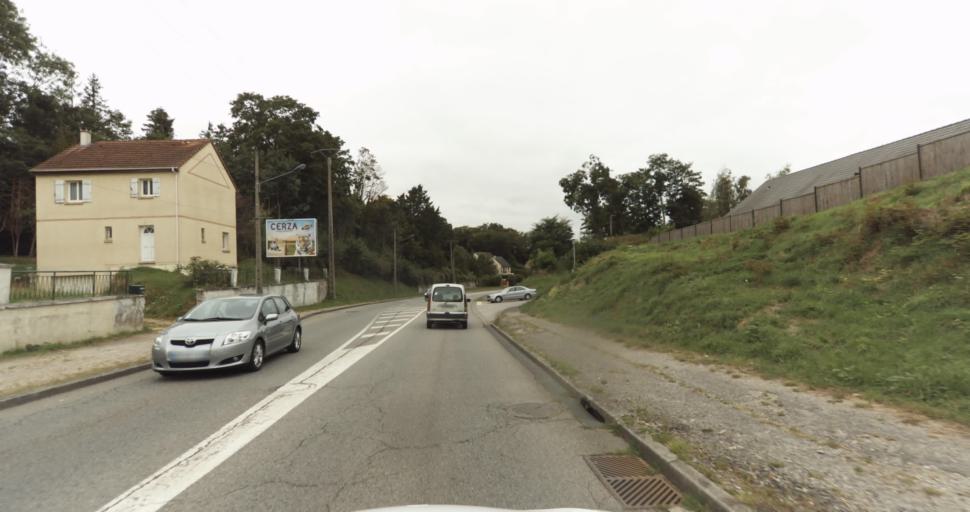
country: FR
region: Haute-Normandie
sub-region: Departement de l'Eure
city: Evreux
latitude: 49.0248
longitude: 1.1676
